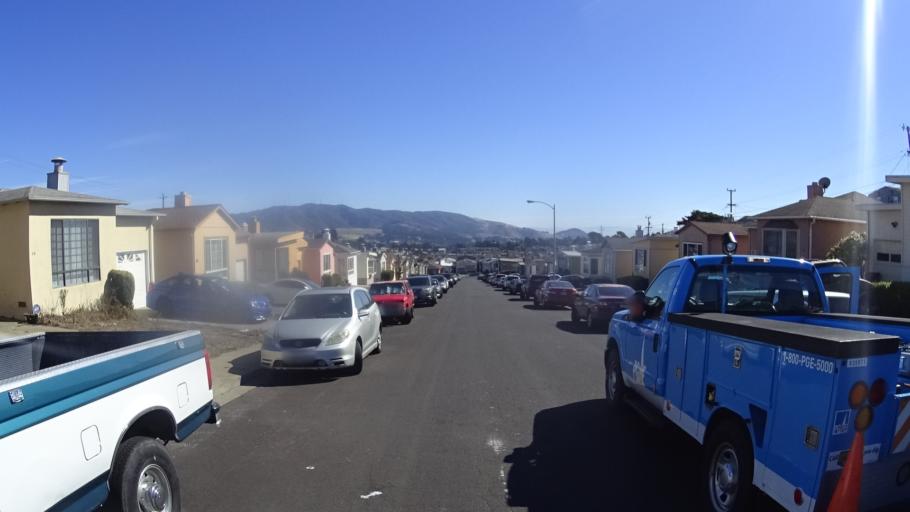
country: US
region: California
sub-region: San Mateo County
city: Broadmoor
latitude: 37.6754
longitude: -122.4874
